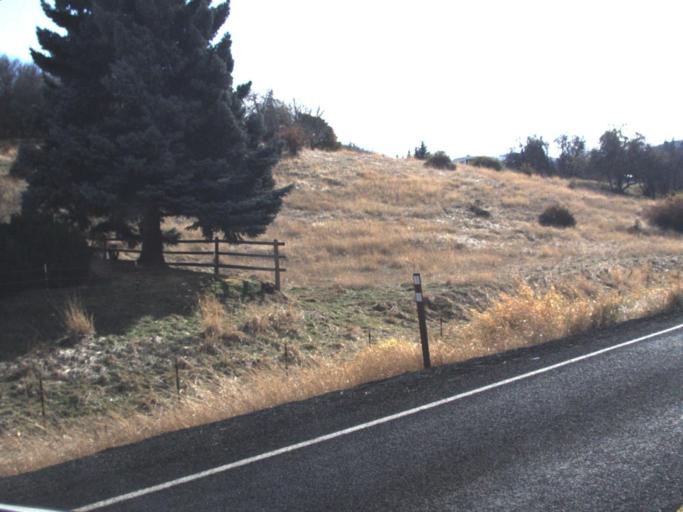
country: US
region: Idaho
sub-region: Latah County
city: Moscow
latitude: 46.9145
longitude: -117.0669
